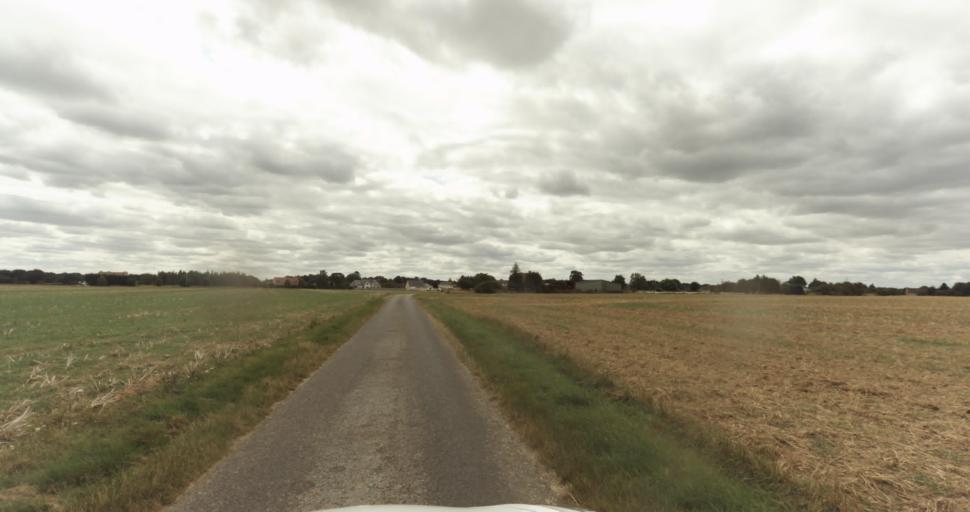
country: FR
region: Haute-Normandie
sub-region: Departement de l'Eure
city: Saint-Germain-sur-Avre
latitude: 48.8061
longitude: 1.2651
